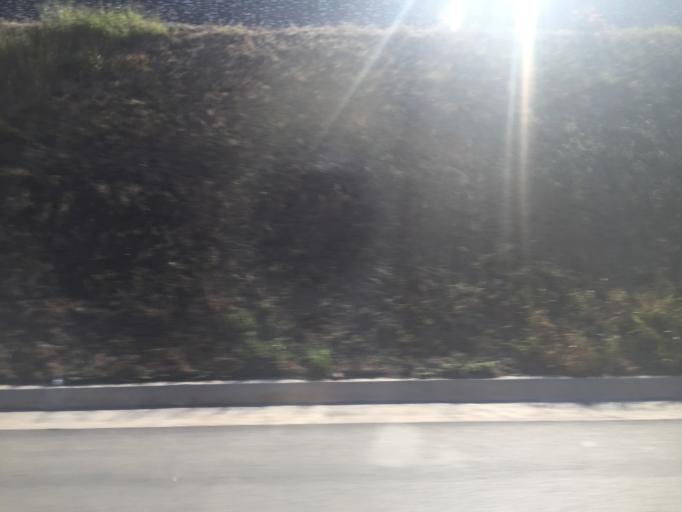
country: TR
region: Bursa
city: Demirtas
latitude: 40.2607
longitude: 29.1158
